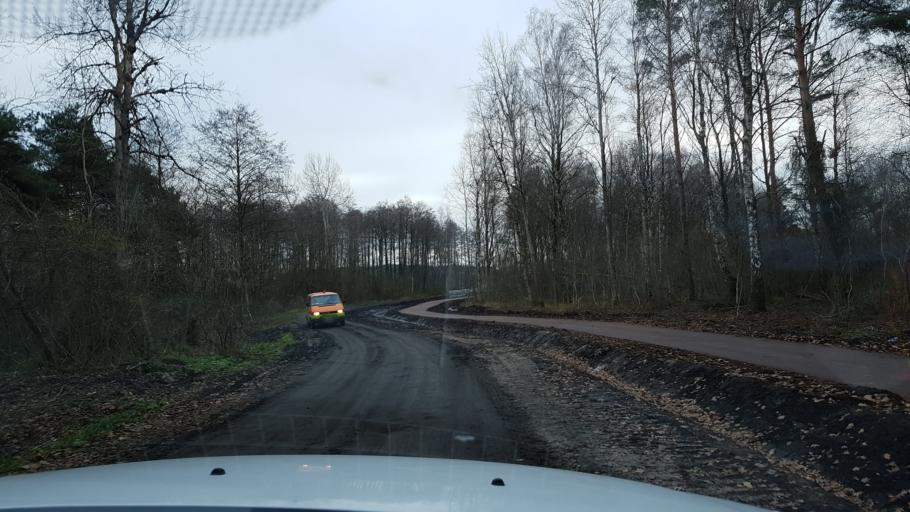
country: PL
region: West Pomeranian Voivodeship
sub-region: Powiat kolobrzeski
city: Grzybowo
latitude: 54.1317
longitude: 15.5157
